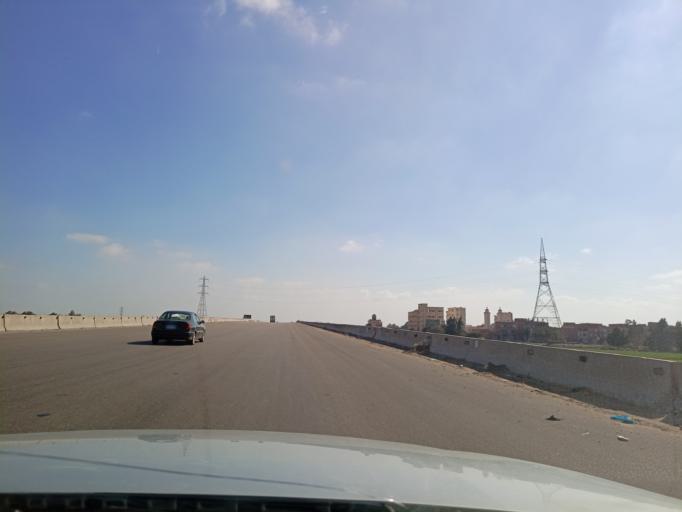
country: EG
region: Eastern Province
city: Mashtul as Suq
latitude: 30.4609
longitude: 31.3295
